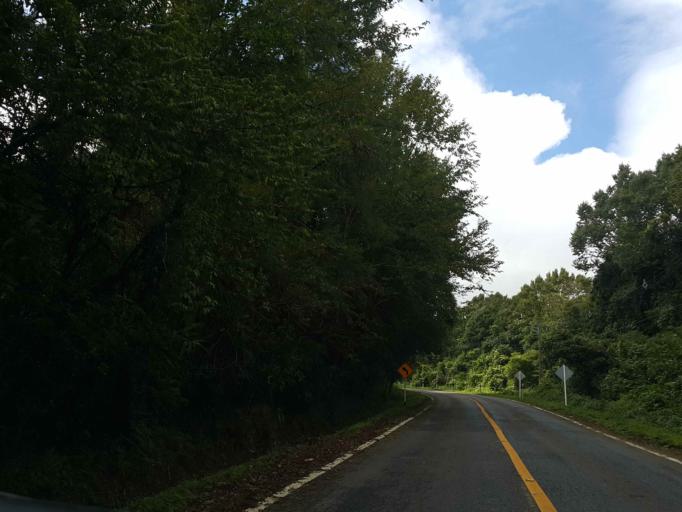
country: TH
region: Chiang Mai
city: Mae Chaem
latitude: 18.5408
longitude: 98.4886
